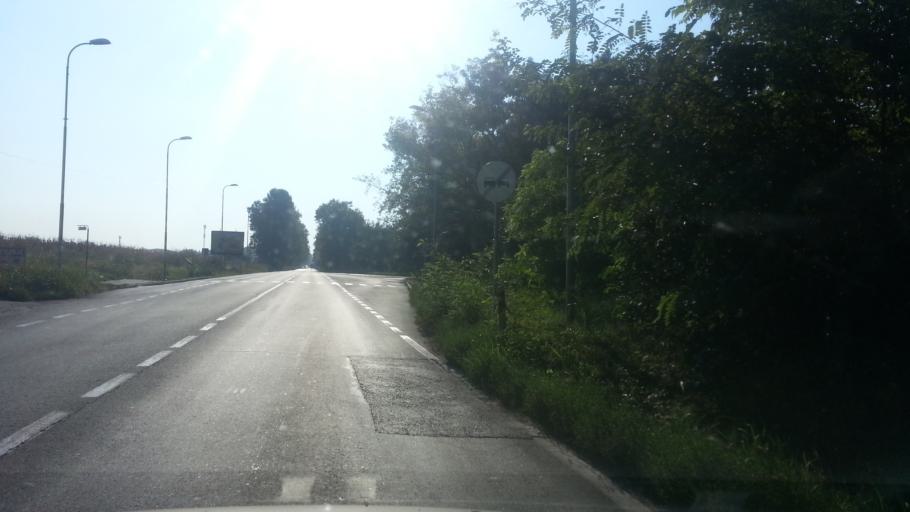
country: RS
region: Central Serbia
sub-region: Belgrade
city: Zemun
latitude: 44.8741
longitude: 20.3433
